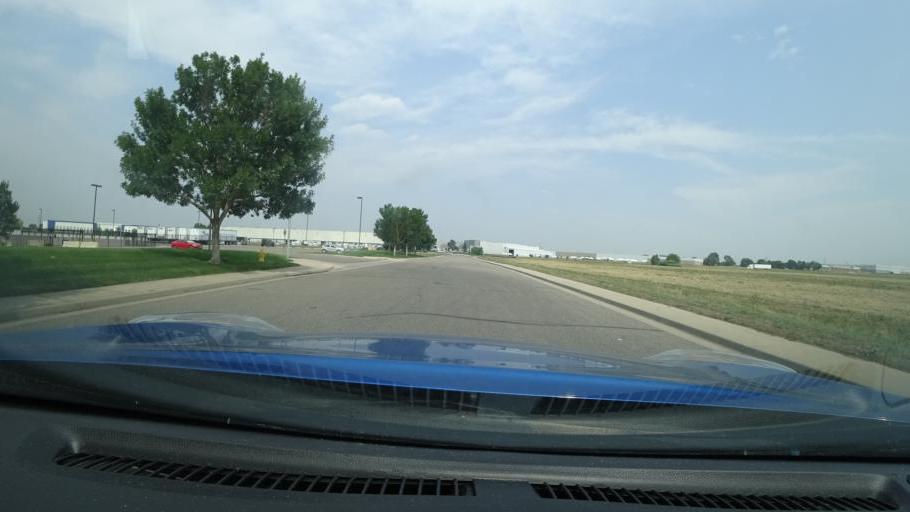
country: US
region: Colorado
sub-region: Adams County
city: Aurora
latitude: 39.7622
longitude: -104.7490
